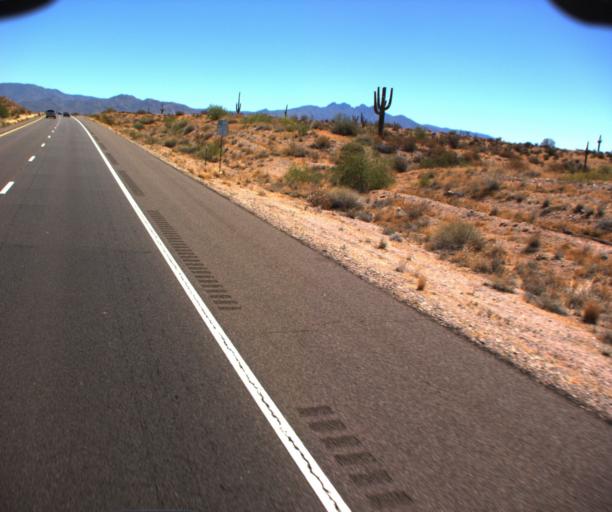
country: US
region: Arizona
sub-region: Maricopa County
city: Rio Verde
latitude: 33.6337
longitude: -111.5498
